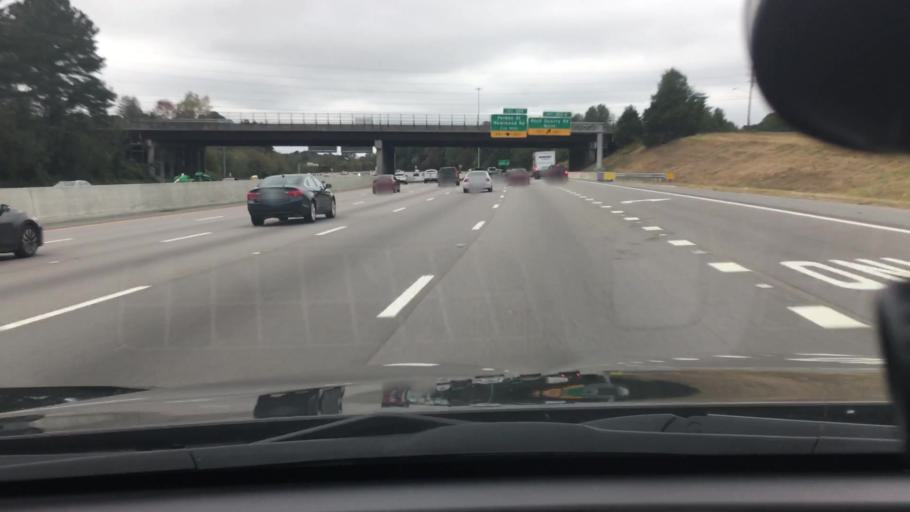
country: US
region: North Carolina
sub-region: Wake County
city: Raleigh
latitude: 35.7581
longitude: -78.6113
